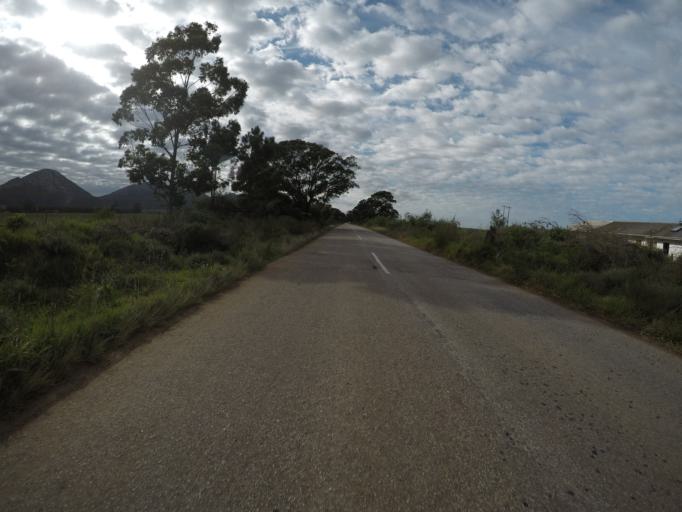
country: ZA
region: Eastern Cape
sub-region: Cacadu District Municipality
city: Kareedouw
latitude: -34.0453
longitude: 24.4459
